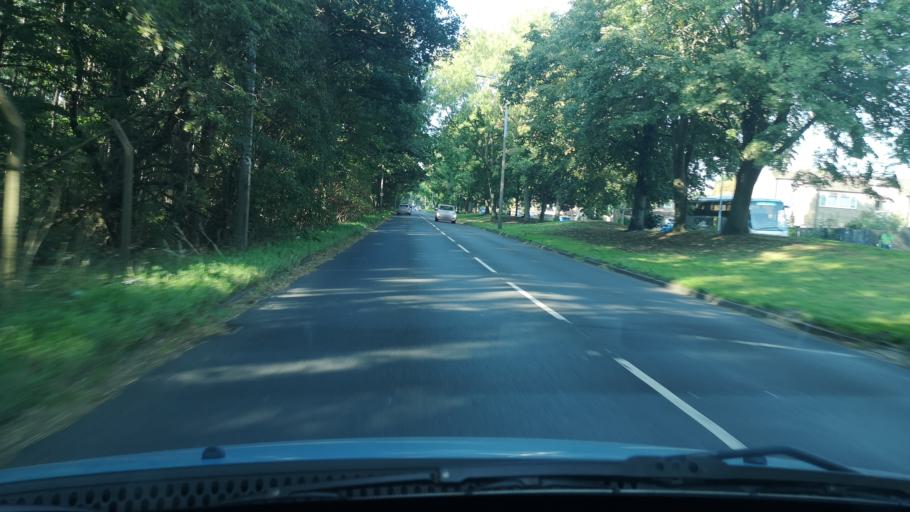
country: GB
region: England
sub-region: North Lincolnshire
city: Scunthorpe
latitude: 53.5775
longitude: -0.6836
